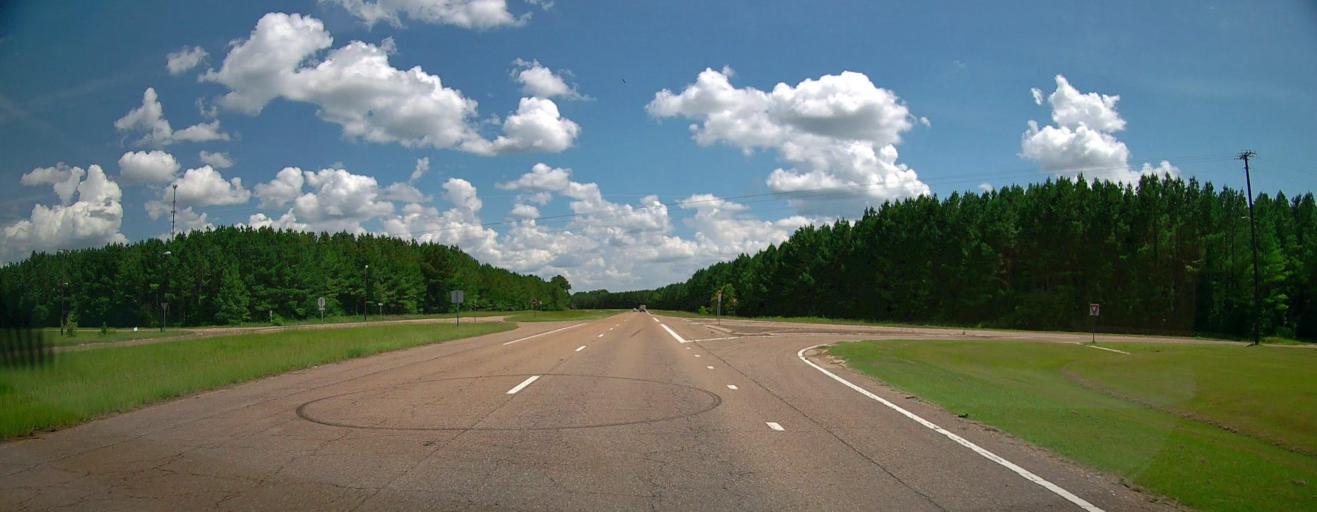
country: US
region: Mississippi
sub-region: Monroe County
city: Aberdeen
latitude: 33.8266
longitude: -88.5855
